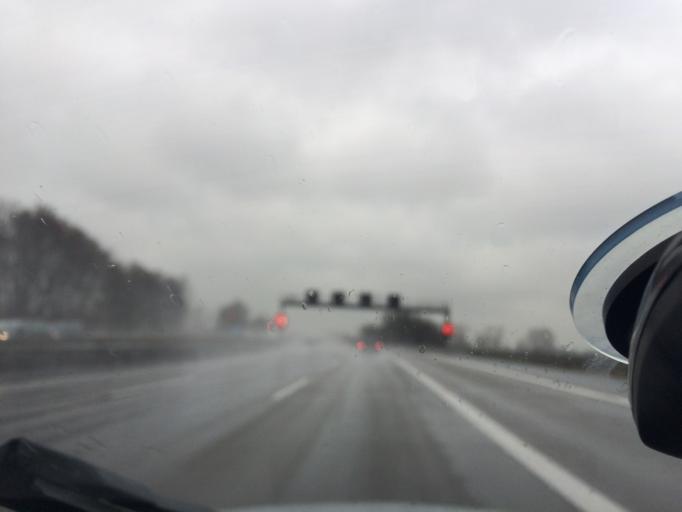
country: DE
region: Hesse
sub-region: Regierungsbezirk Darmstadt
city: Bad Homburg vor der Hoehe
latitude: 50.2081
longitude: 8.6573
